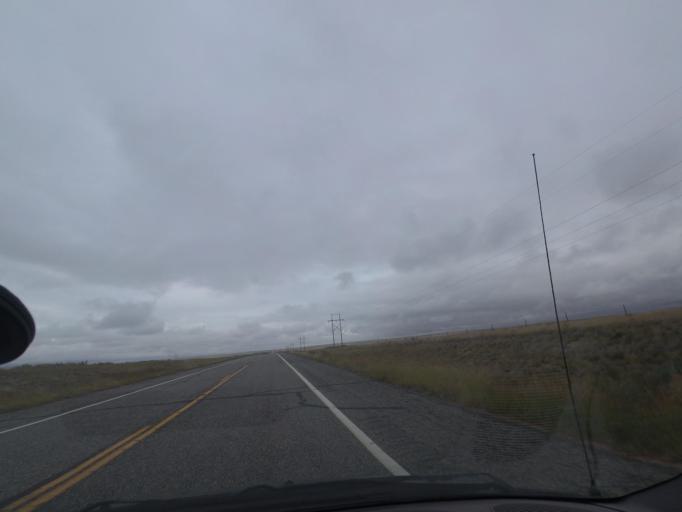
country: US
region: Colorado
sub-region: Washington County
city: Akron
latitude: 39.7395
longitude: -103.4351
